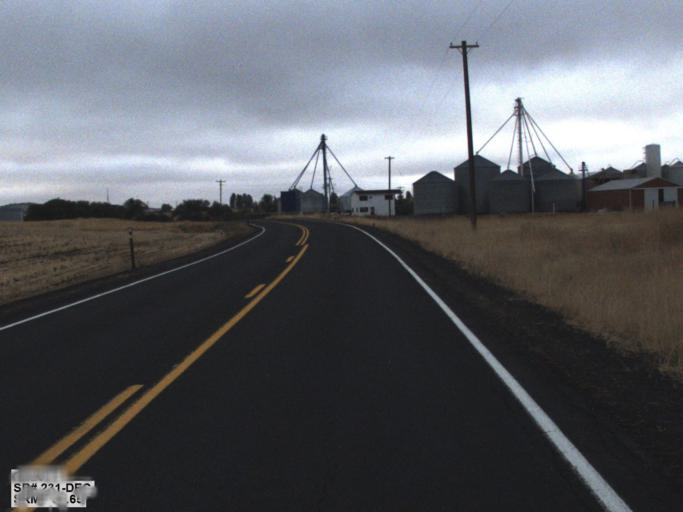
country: US
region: Washington
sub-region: Spokane County
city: Medical Lake
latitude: 47.6918
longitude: -117.8820
